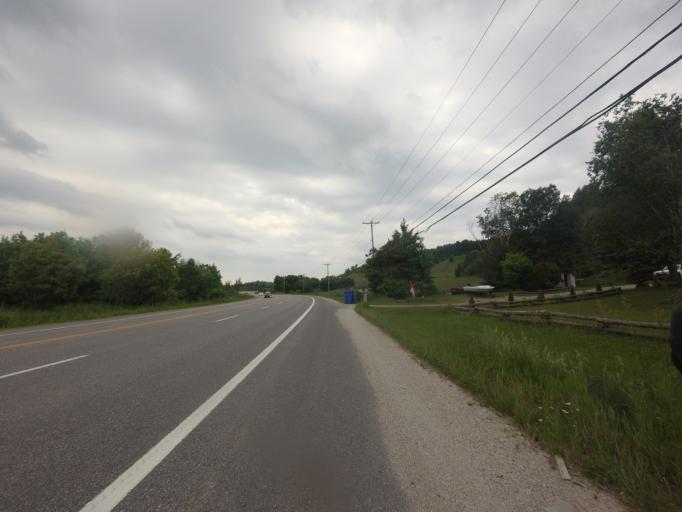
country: CA
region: Quebec
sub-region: Outaouais
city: Wakefield
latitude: 45.7107
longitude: -75.9202
